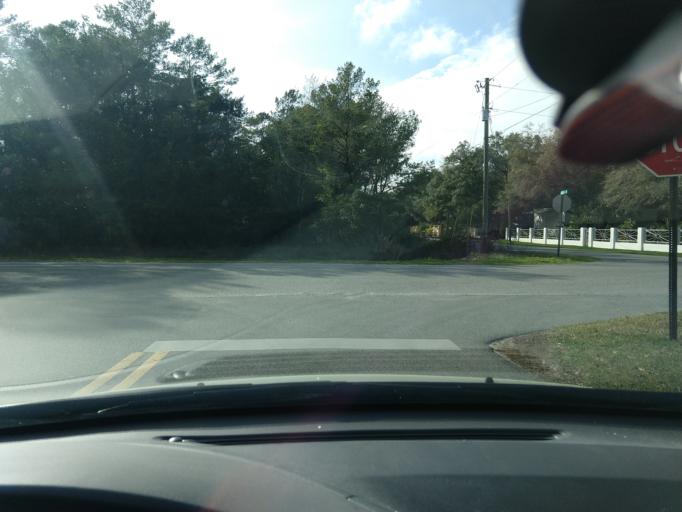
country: US
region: Florida
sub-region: Walton County
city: Seaside
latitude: 30.3788
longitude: -86.1536
